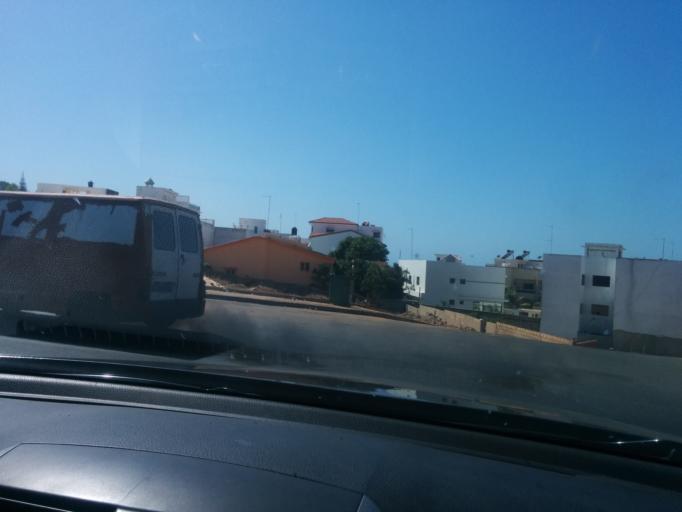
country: SN
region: Dakar
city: Mermoz Boabab
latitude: 14.7095
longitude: -17.4866
